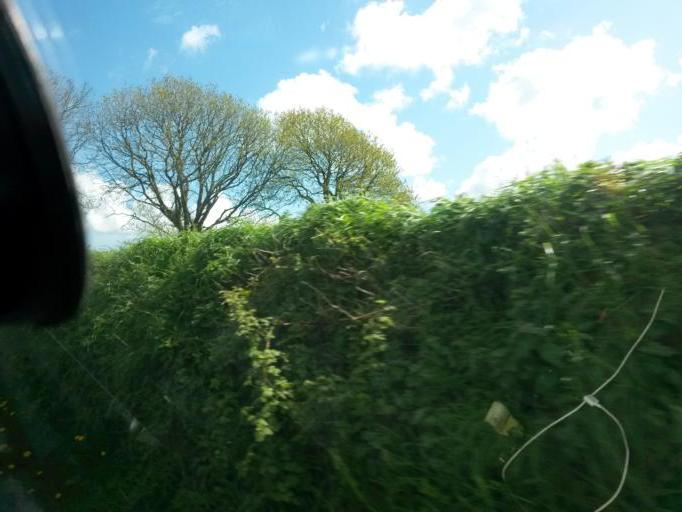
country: IE
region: Munster
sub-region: Waterford
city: Dunmore East
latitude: 52.2444
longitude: -6.9920
